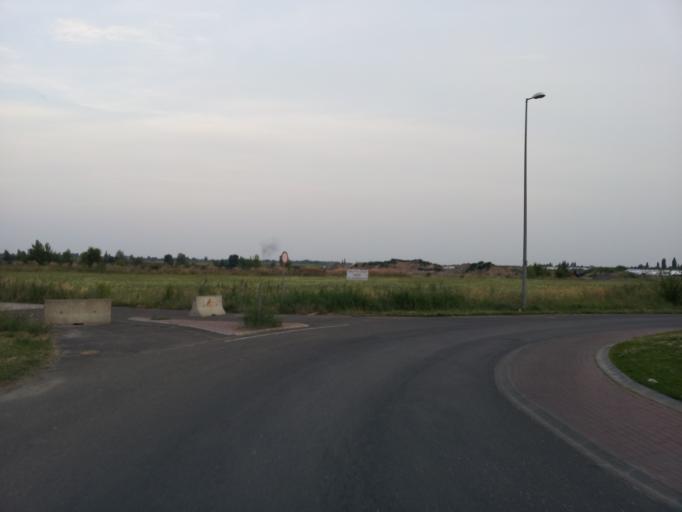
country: HU
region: Pest
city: Szigetszentmiklos
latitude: 47.3701
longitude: 19.0486
